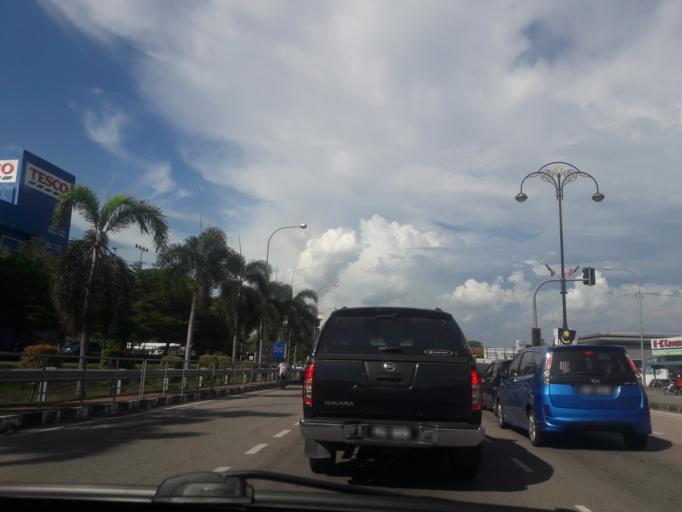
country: MY
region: Kedah
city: Sungai Petani
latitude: 5.6224
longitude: 100.4768
